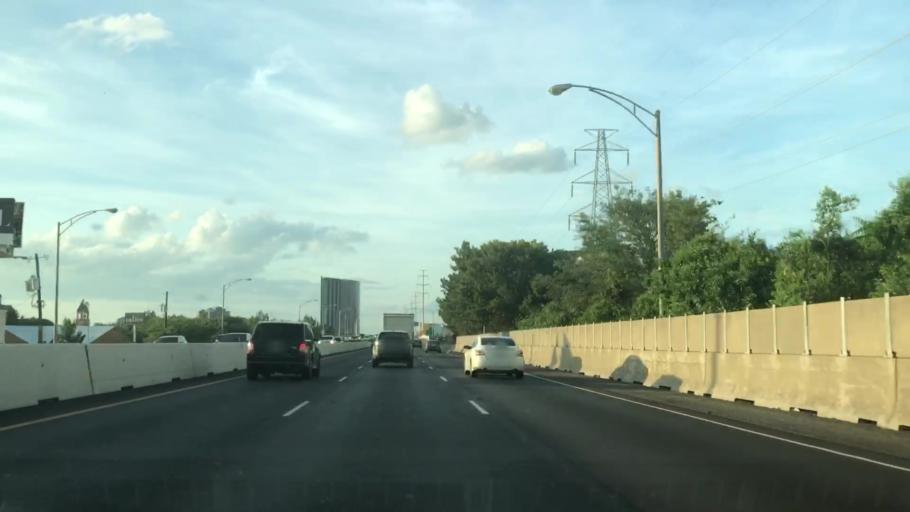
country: US
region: Texas
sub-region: Dallas County
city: Addison
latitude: 32.9166
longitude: -96.8170
